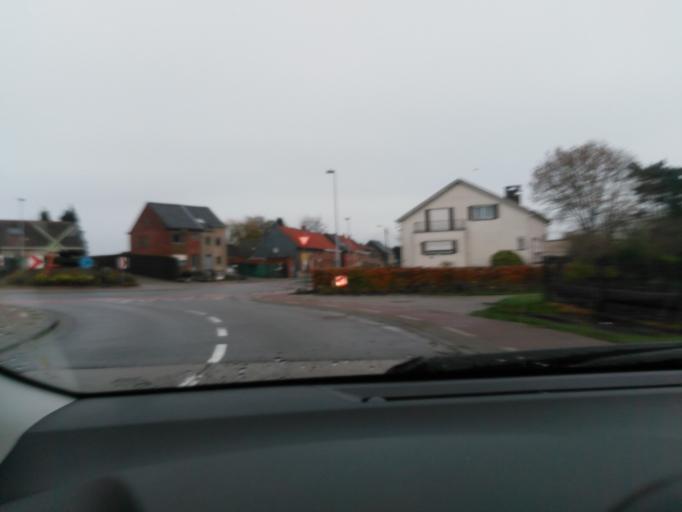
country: BE
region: Flanders
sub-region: Provincie Oost-Vlaanderen
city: Sint-Gillis-Waas
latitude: 51.2550
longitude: 4.0931
